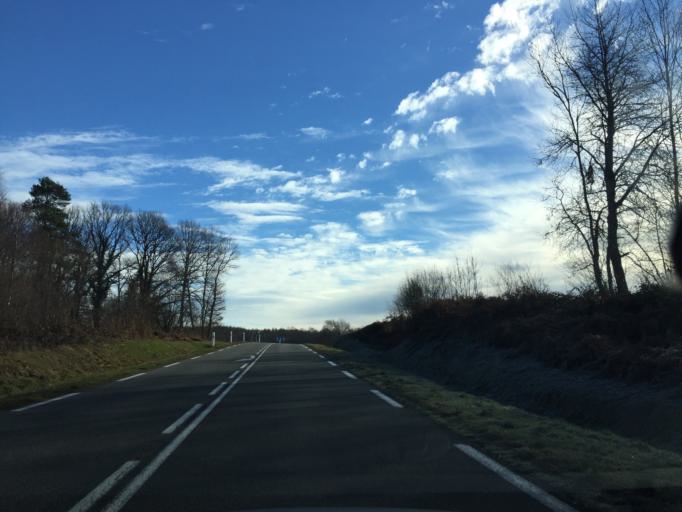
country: FR
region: Limousin
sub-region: Departement de la Creuse
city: Auzances
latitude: 45.8847
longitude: 2.4965
